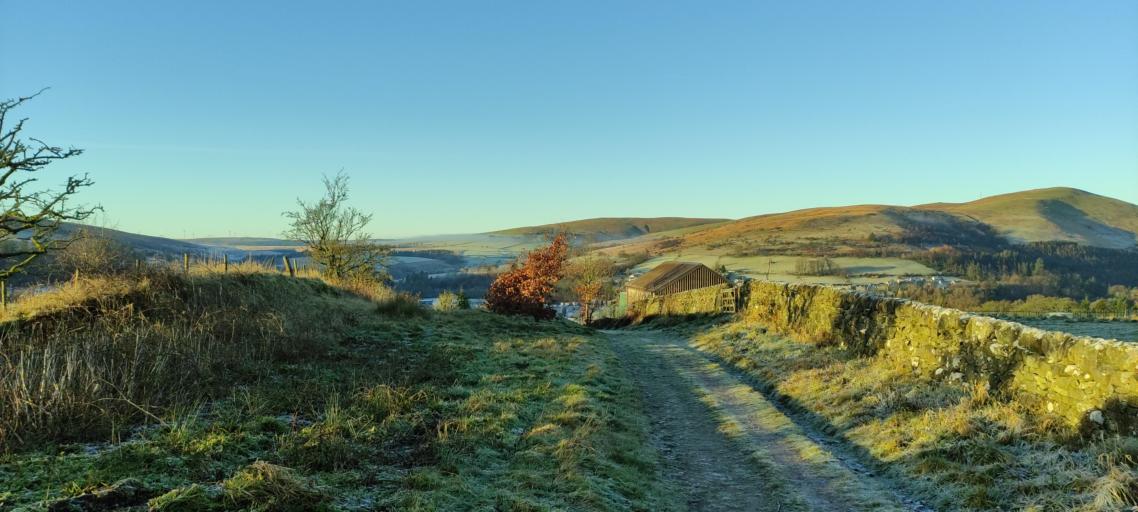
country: GB
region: Scotland
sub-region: Dumfries and Galloway
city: Langholm
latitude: 55.1536
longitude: -2.9920
